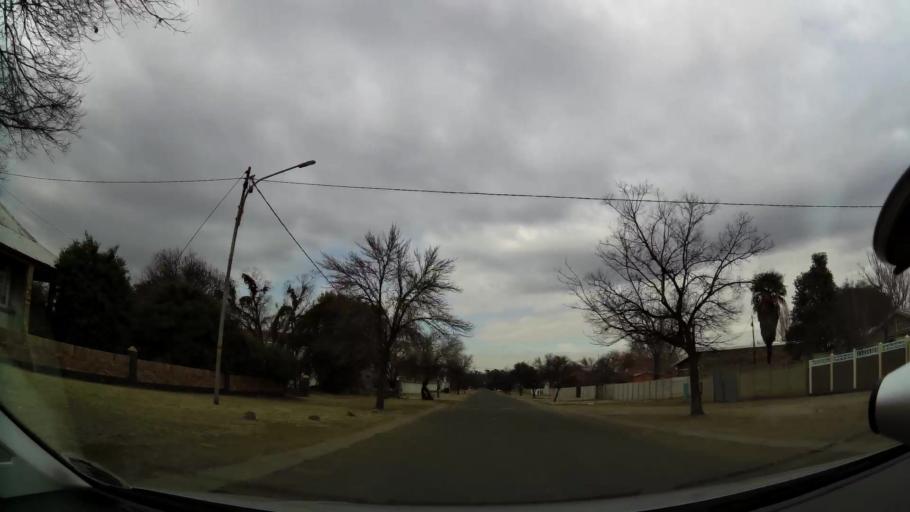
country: ZA
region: Orange Free State
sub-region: Fezile Dabi District Municipality
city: Kroonstad
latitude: -27.6564
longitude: 27.2411
